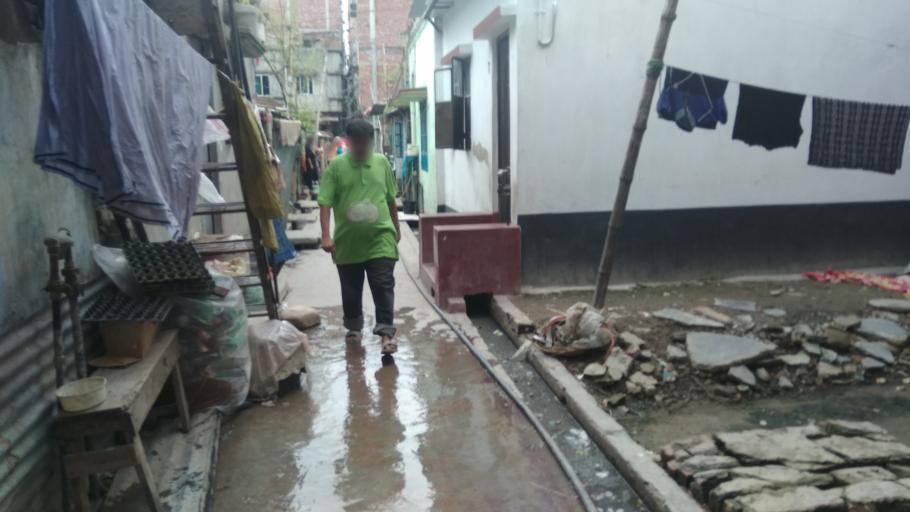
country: BD
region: Dhaka
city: Tungi
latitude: 23.8195
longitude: 90.3788
